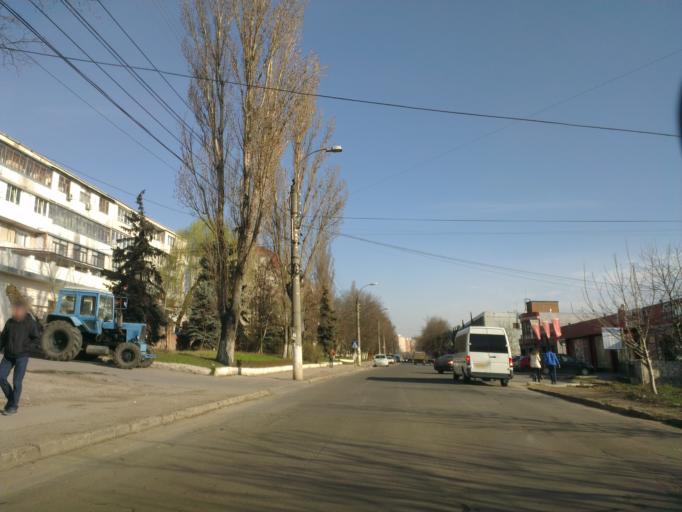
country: MD
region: Chisinau
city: Chisinau
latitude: 47.0231
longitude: 28.8832
